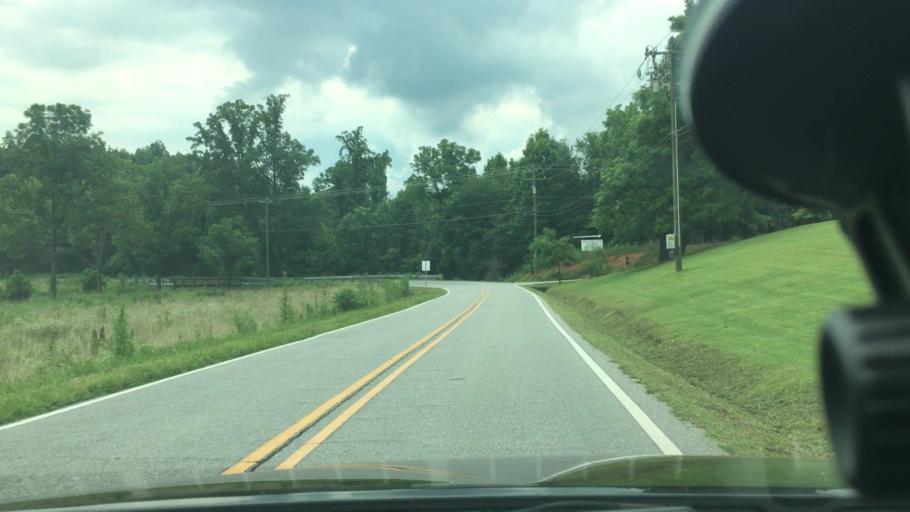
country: US
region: North Carolina
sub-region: McDowell County
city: West Marion
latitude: 35.6409
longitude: -82.0140
